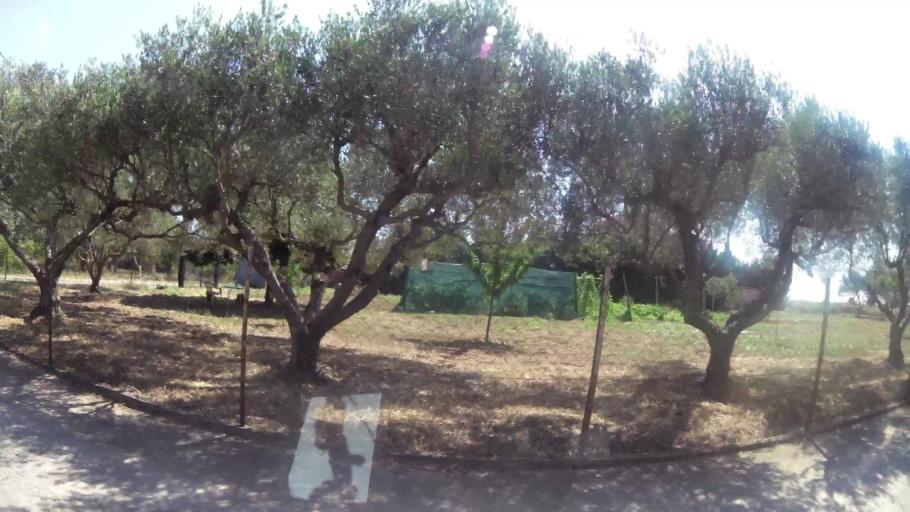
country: GR
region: Central Macedonia
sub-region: Nomos Thessalonikis
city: Agia Triada
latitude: 40.4955
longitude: 22.8917
